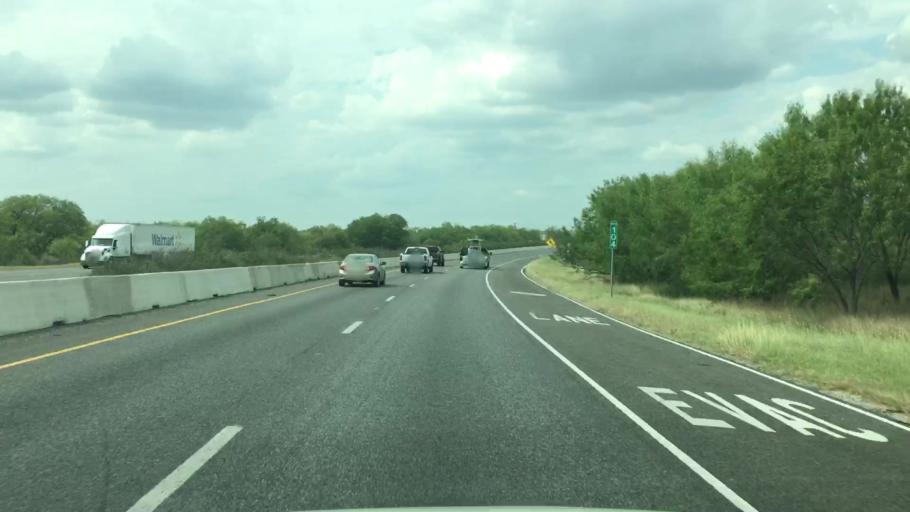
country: US
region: Texas
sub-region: Atascosa County
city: Pleasanton
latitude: 28.9098
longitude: -98.4337
